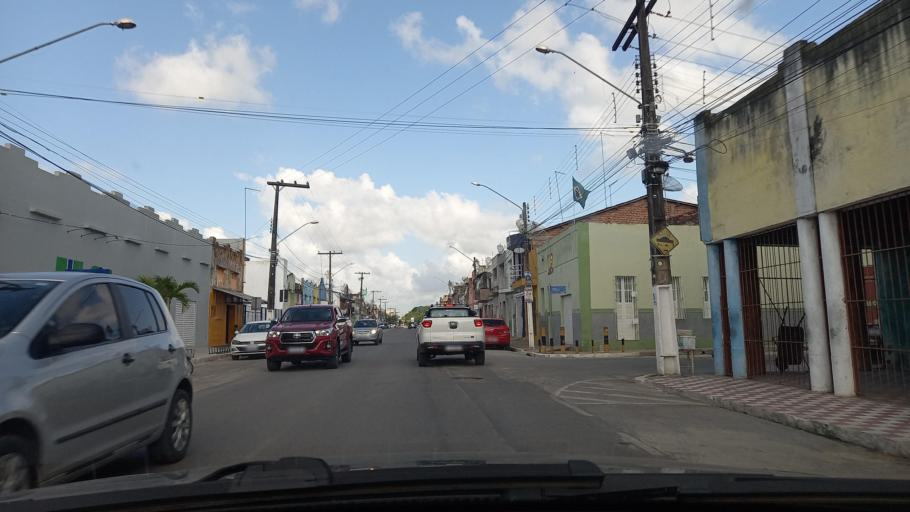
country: BR
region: Pernambuco
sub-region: Goiana
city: Goiana
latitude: -7.5591
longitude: -34.9954
